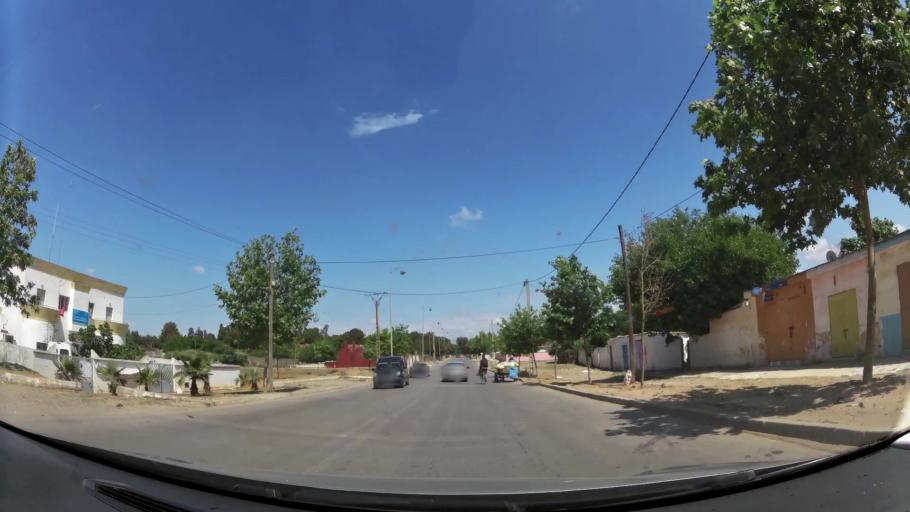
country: MA
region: Gharb-Chrarda-Beni Hssen
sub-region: Kenitra Province
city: Kenitra
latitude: 34.2330
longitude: -6.5398
